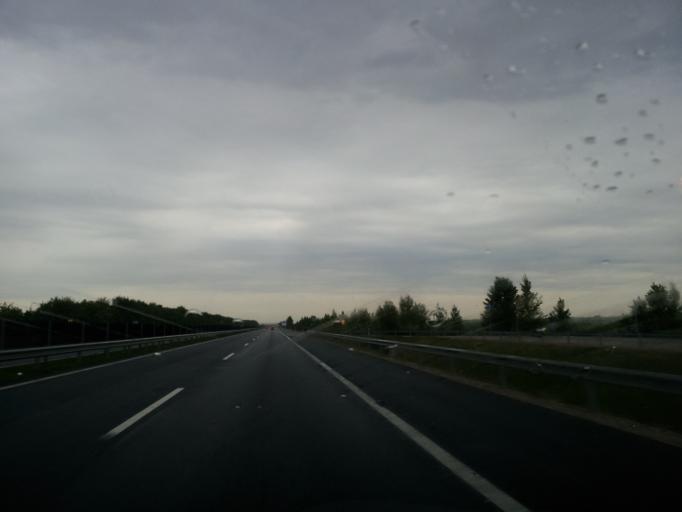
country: HU
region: Fejer
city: Rackeresztur
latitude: 47.2861
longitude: 18.8632
